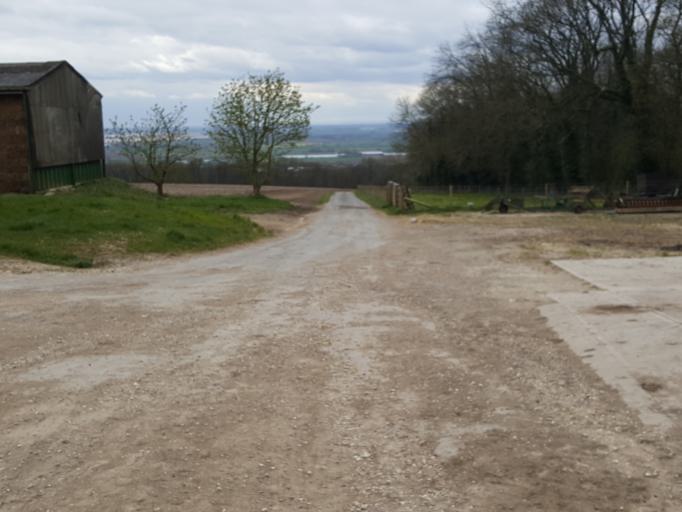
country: GB
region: England
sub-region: East Riding of Yorkshire
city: Brantingham
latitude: 53.7687
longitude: -0.5829
